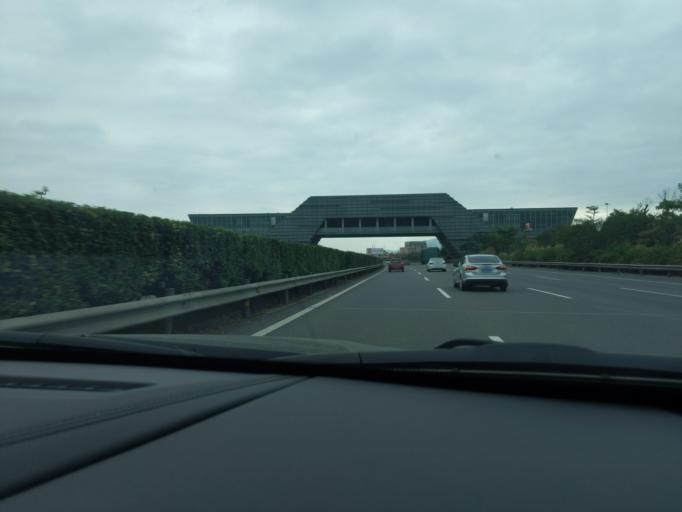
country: CN
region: Fujian
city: Neikeng
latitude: 24.7488
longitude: 118.4345
